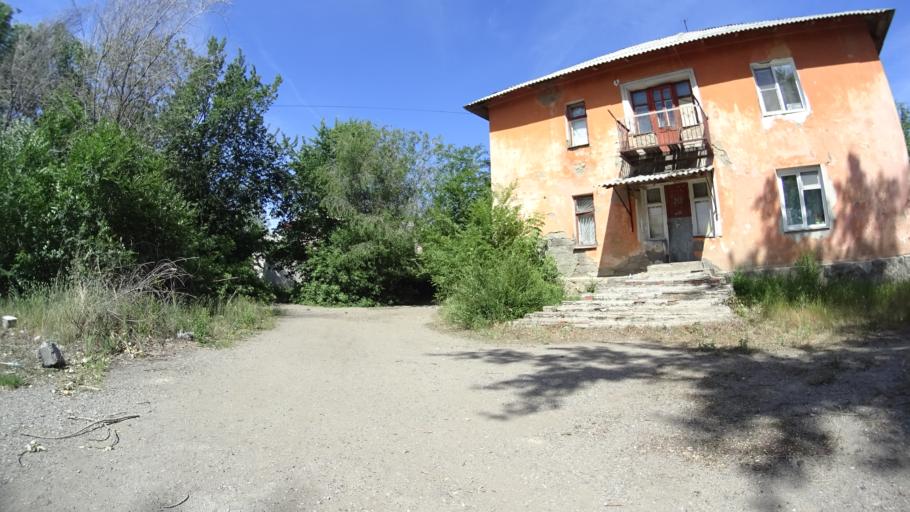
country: RU
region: Chelyabinsk
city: Troitsk
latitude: 54.0441
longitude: 61.6324
